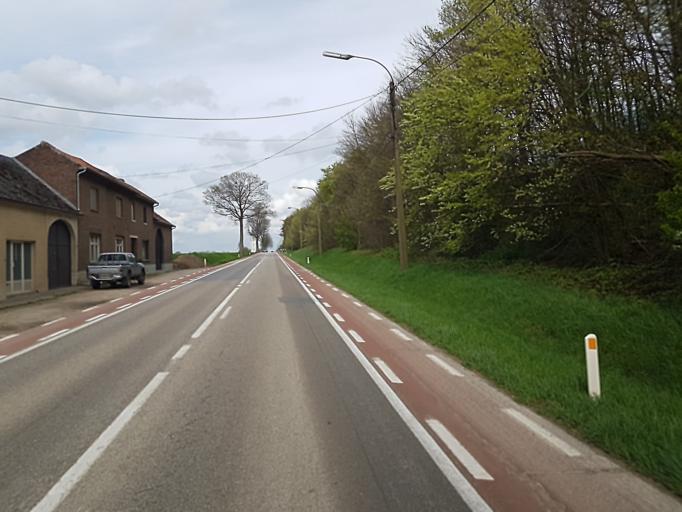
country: BE
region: Flanders
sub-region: Provincie Limburg
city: Riemst
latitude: 50.8498
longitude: 5.6253
